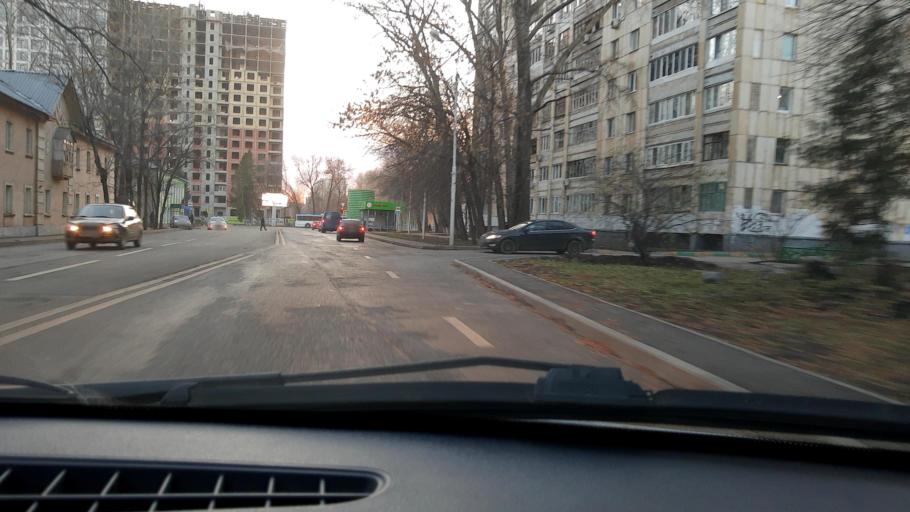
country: RU
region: Bashkortostan
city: Avdon
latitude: 54.6980
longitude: 55.8277
